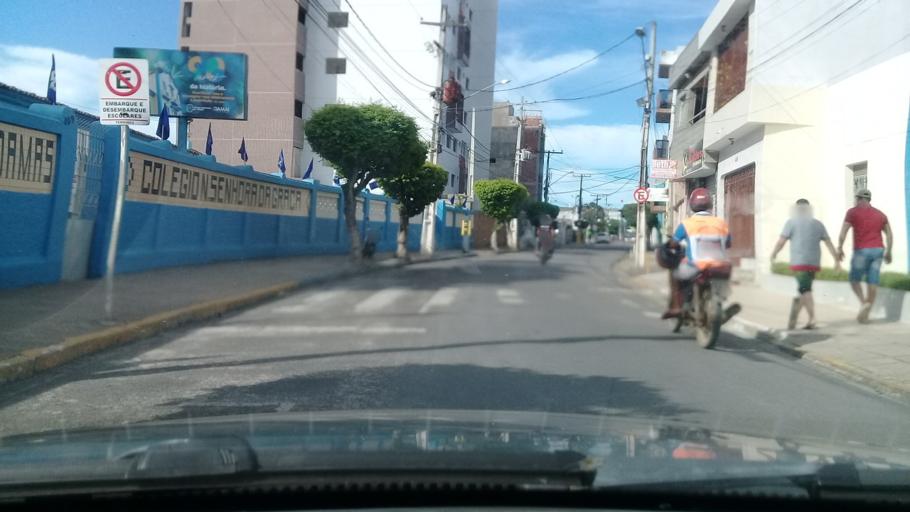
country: BR
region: Pernambuco
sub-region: Vitoria De Santo Antao
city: Vitoria de Santo Antao
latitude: -8.1158
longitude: -35.2942
